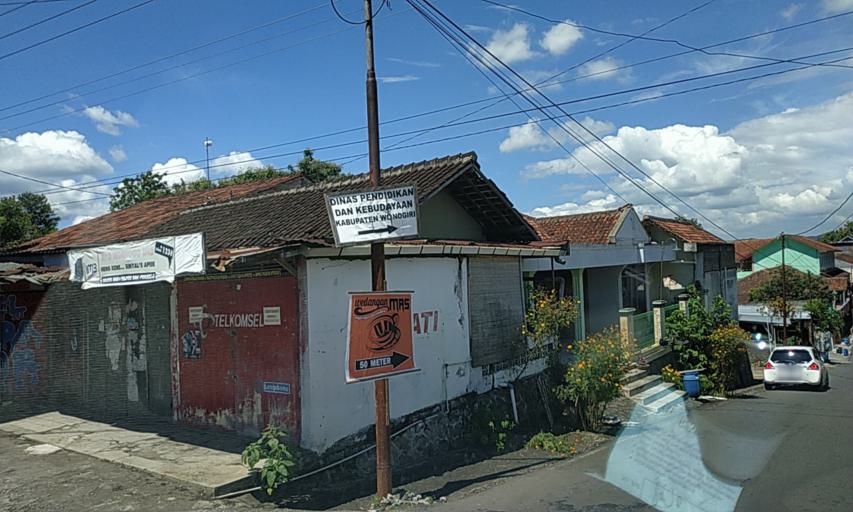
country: ID
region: Central Java
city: Selogiri
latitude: -7.8115
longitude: 110.9507
